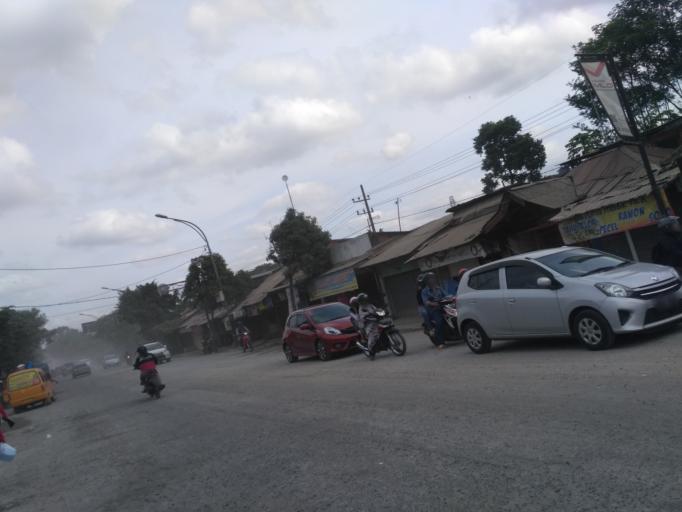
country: ID
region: East Java
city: Kebonsari
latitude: -8.0231
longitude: 112.6277
